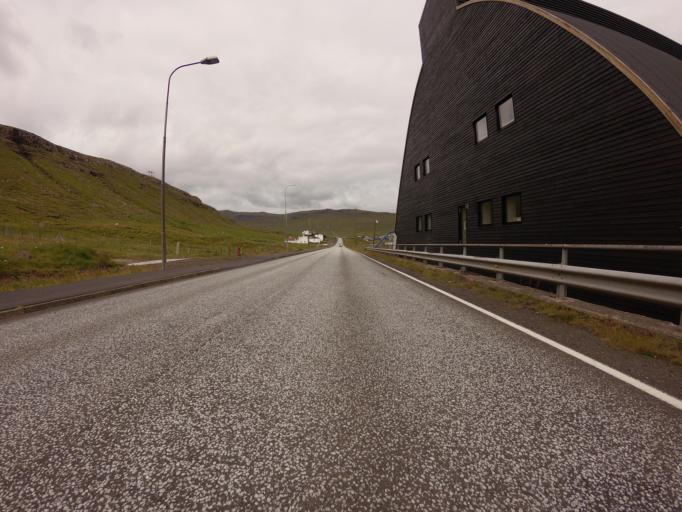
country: FO
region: Suduroy
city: Tvoroyri
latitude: 61.5518
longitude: -6.8291
